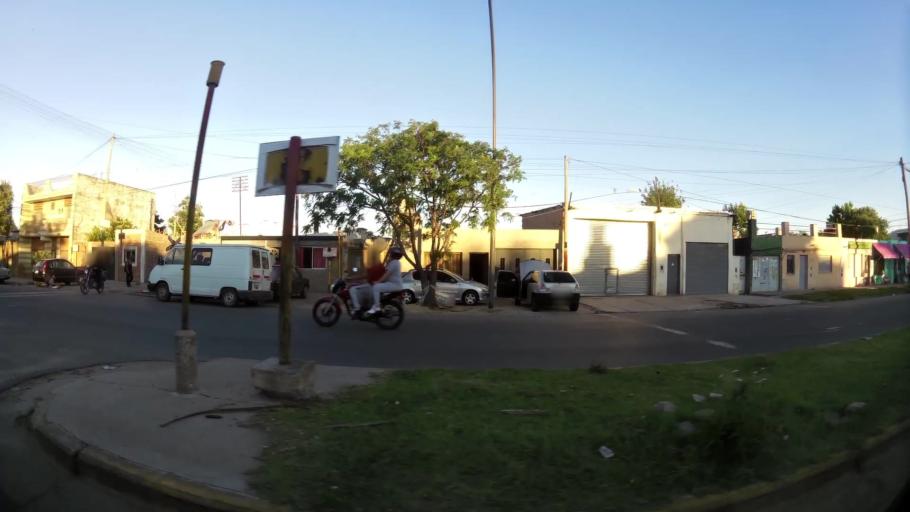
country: AR
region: Santa Fe
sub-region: Departamento de Rosario
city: Rosario
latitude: -32.9622
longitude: -60.6850
